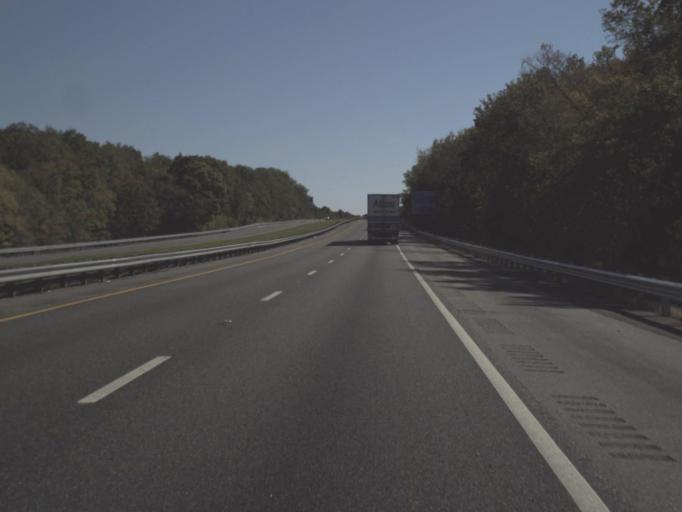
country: US
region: Florida
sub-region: Sumter County
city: Wildwood
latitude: 28.8414
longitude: -82.0574
